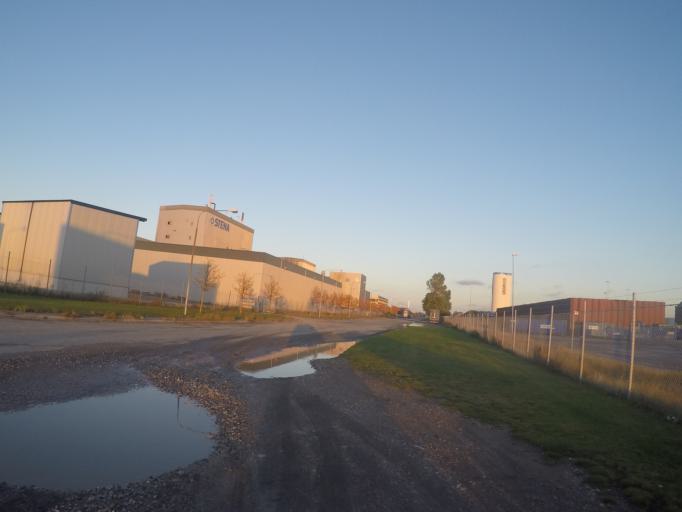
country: SE
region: Skane
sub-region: Malmo
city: Malmoe
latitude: 55.6270
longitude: 13.0044
